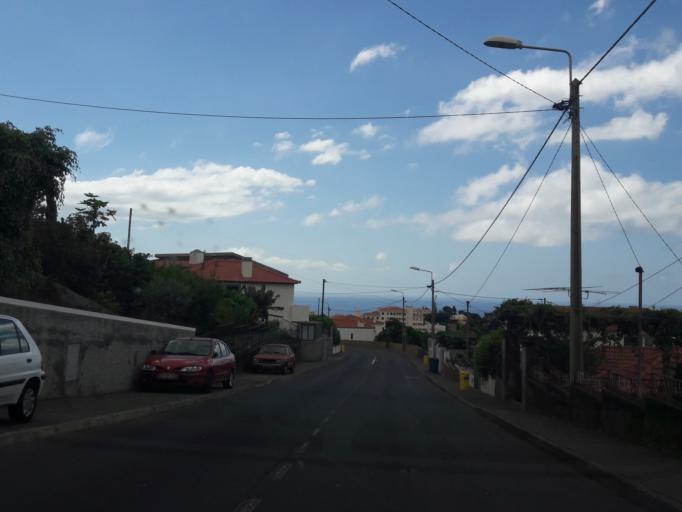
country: PT
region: Madeira
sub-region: Funchal
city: Nossa Senhora do Monte
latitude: 32.6621
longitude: -16.9234
